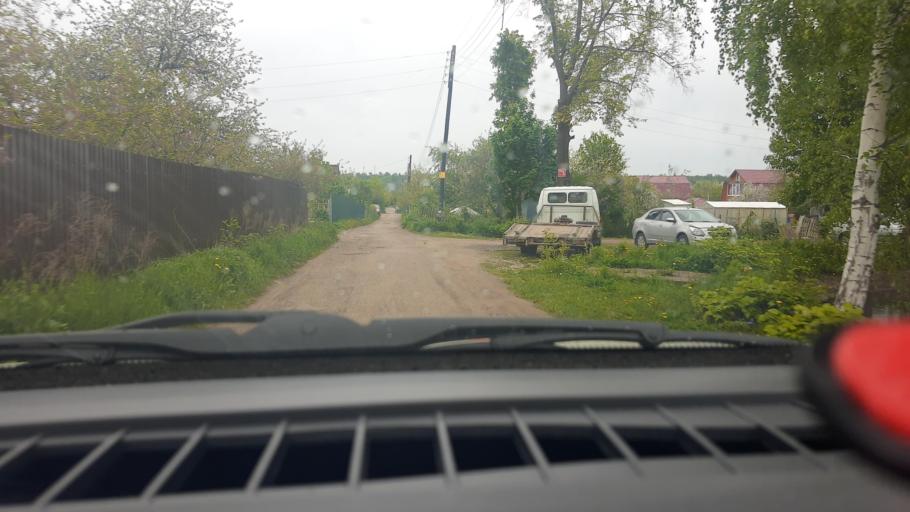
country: RU
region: Nizjnij Novgorod
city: Burevestnik
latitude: 56.2164
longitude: 43.8514
